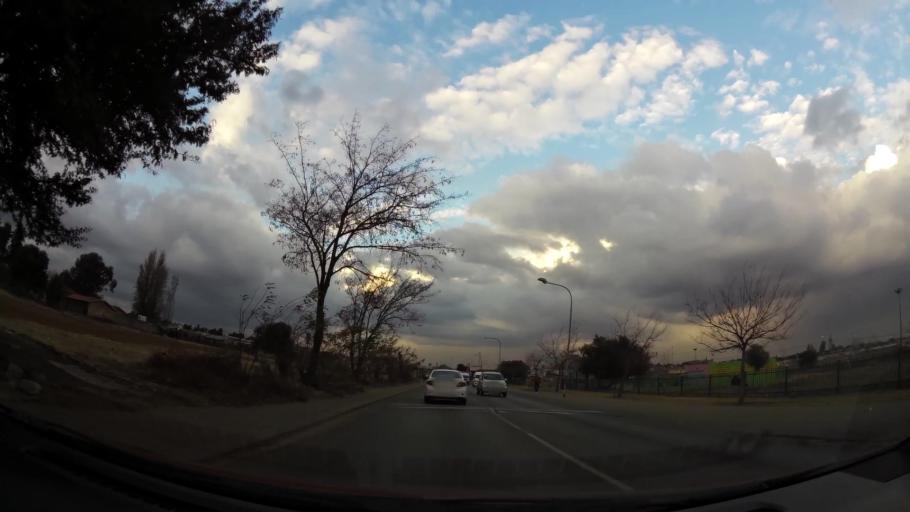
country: ZA
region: Gauteng
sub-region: City of Johannesburg Metropolitan Municipality
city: Soweto
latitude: -26.2406
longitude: 27.8440
